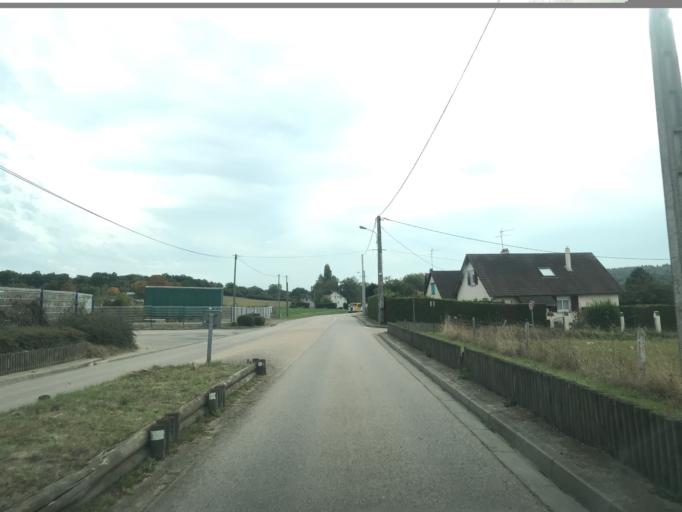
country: FR
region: Haute-Normandie
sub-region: Departement de l'Eure
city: Acquigny
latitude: 49.1951
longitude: 1.1850
